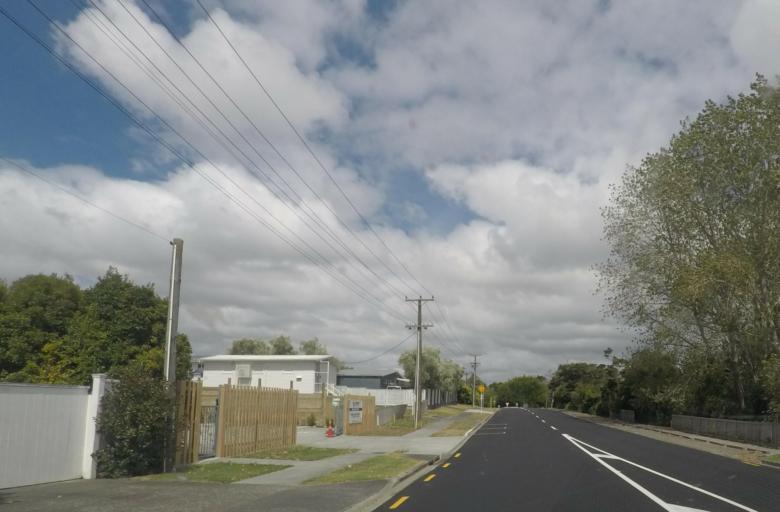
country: NZ
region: Auckland
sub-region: Auckland
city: North Shore
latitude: -36.7728
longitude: 174.6767
